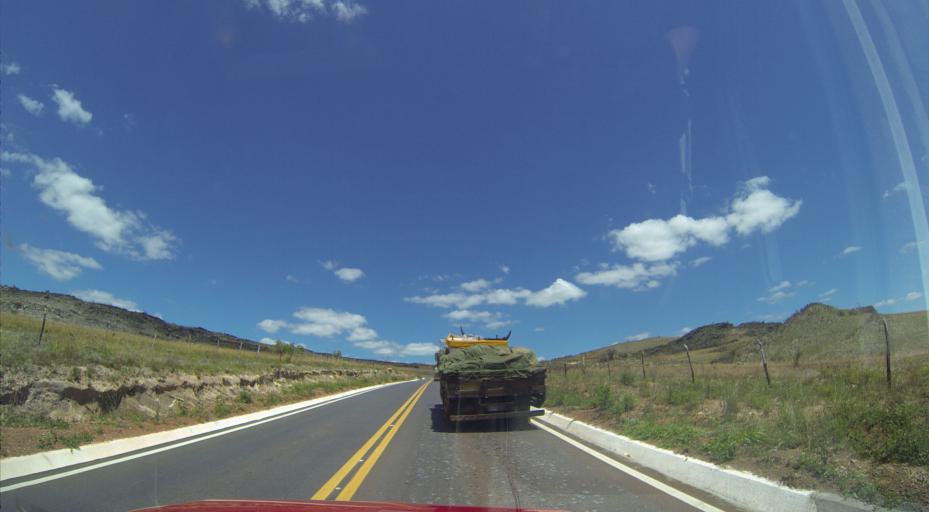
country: BR
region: Minas Gerais
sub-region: Conceicao Do Mato Dentro
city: Conceicao do Mato Dentro
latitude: -19.2838
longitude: -43.5792
